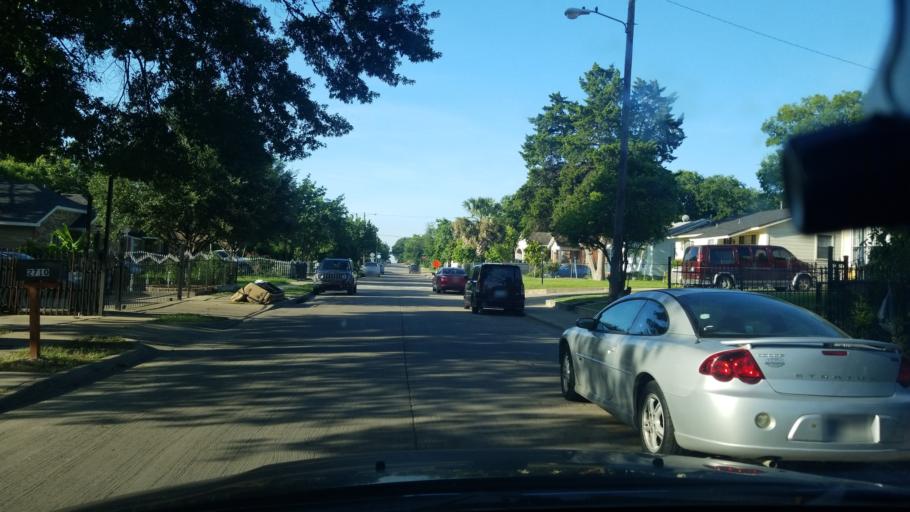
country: US
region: Texas
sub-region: Dallas County
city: Dallas
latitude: 32.7147
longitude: -96.8182
